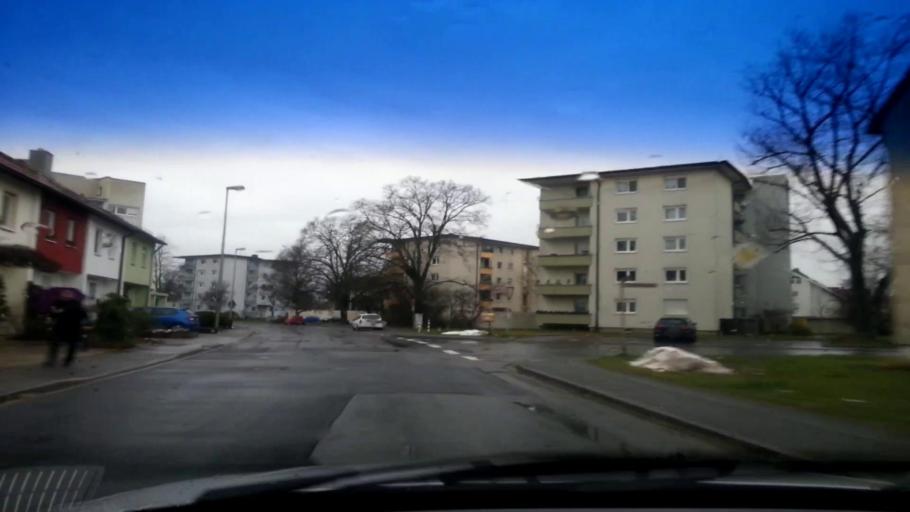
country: DE
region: Bavaria
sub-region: Upper Franconia
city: Gundelsheim
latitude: 49.9245
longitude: 10.9275
